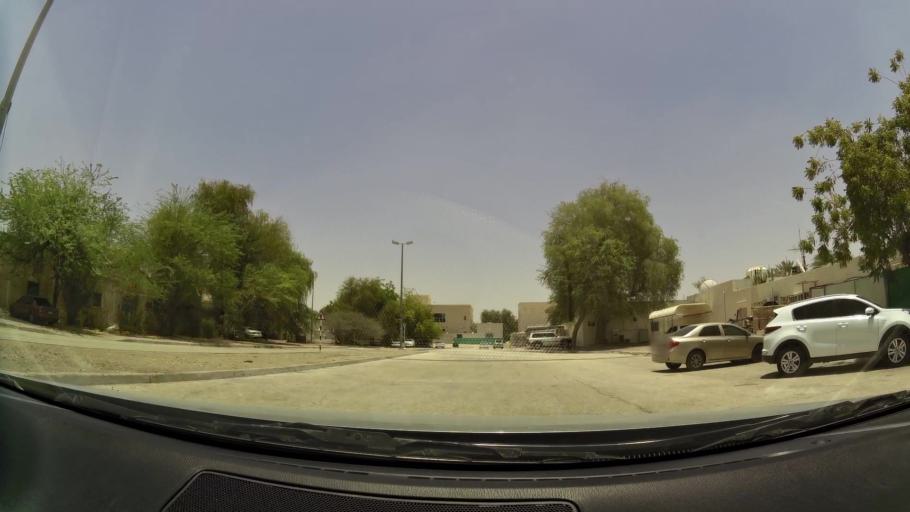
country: OM
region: Al Buraimi
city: Al Buraymi
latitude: 24.2621
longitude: 55.7348
